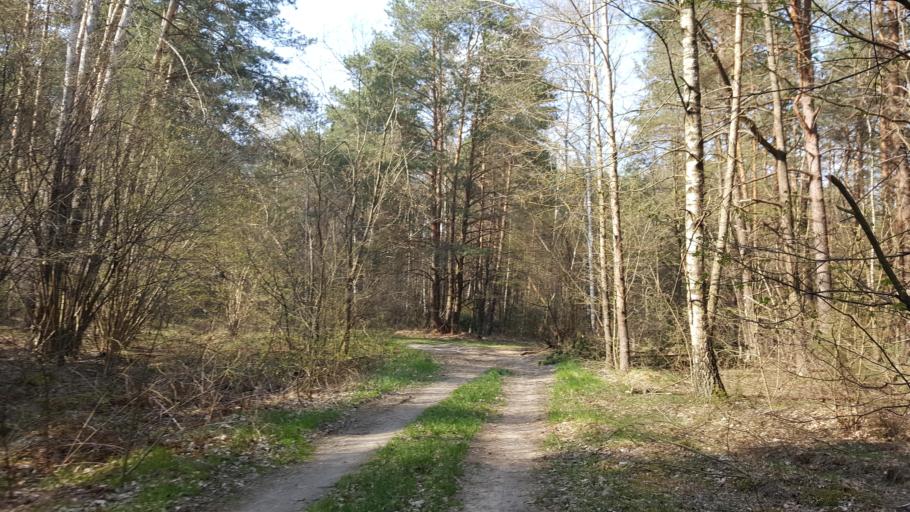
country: BY
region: Brest
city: Kamyanyets
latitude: 52.3408
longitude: 23.8486
